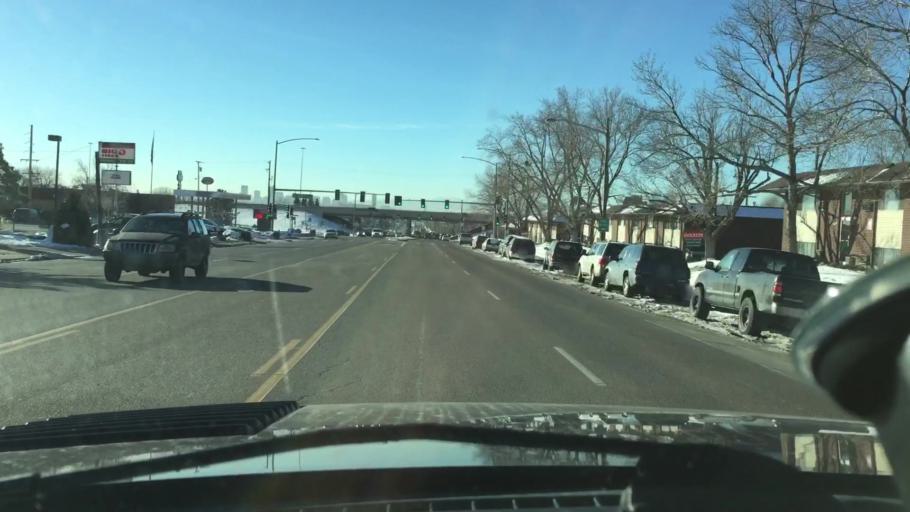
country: US
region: Colorado
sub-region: Adams County
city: Sherrelwood
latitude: 39.8335
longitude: -105.0062
